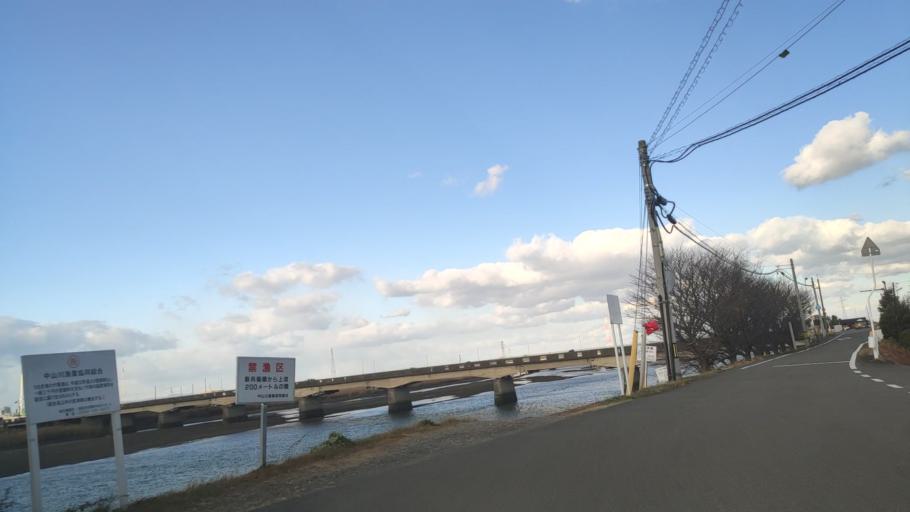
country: JP
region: Ehime
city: Saijo
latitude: 33.9072
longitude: 133.1291
